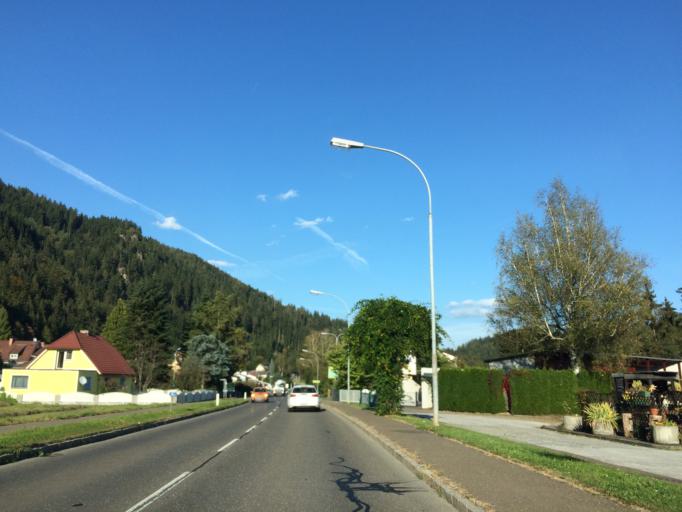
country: AT
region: Styria
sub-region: Politischer Bezirk Leoben
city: Leoben
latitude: 47.3601
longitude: 15.0624
